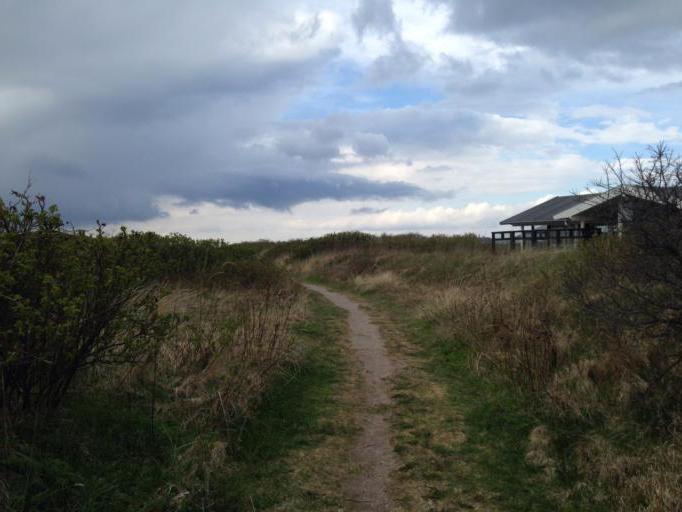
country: DK
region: North Denmark
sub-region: Hjorring Kommune
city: Hjorring
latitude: 57.4909
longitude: 9.8352
